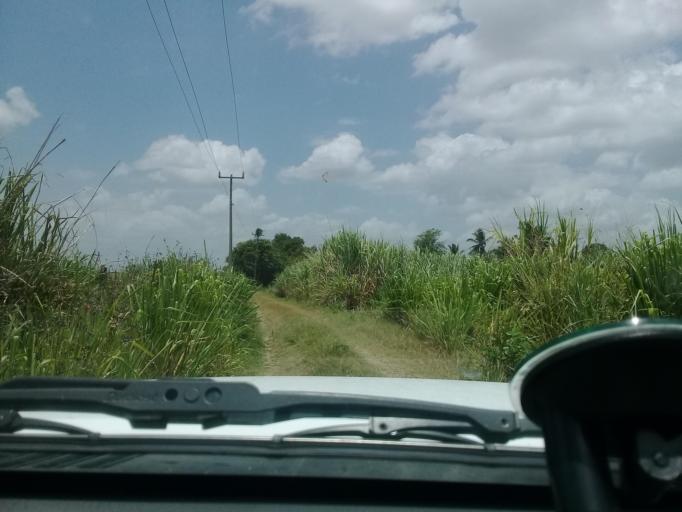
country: MX
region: Veracruz
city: Moralillo
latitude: 22.1348
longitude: -98.0390
